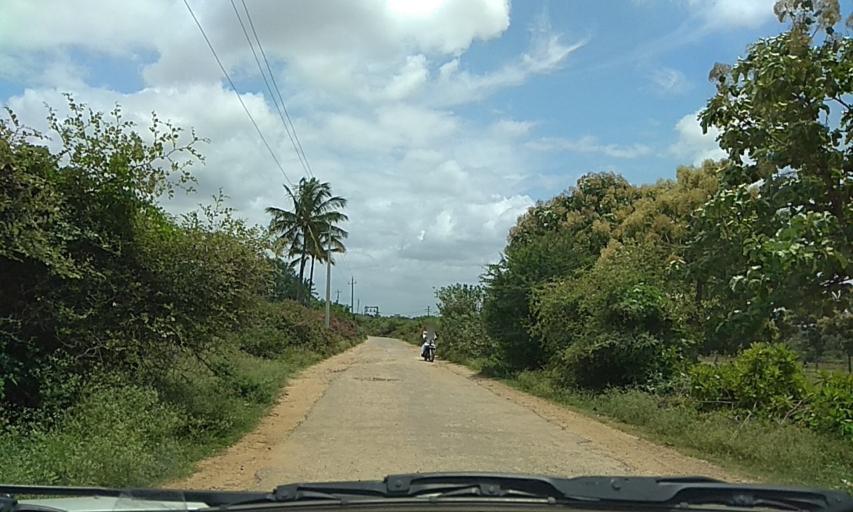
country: IN
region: Karnataka
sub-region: Chamrajnagar
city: Gundlupet
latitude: 11.8867
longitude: 76.6878
